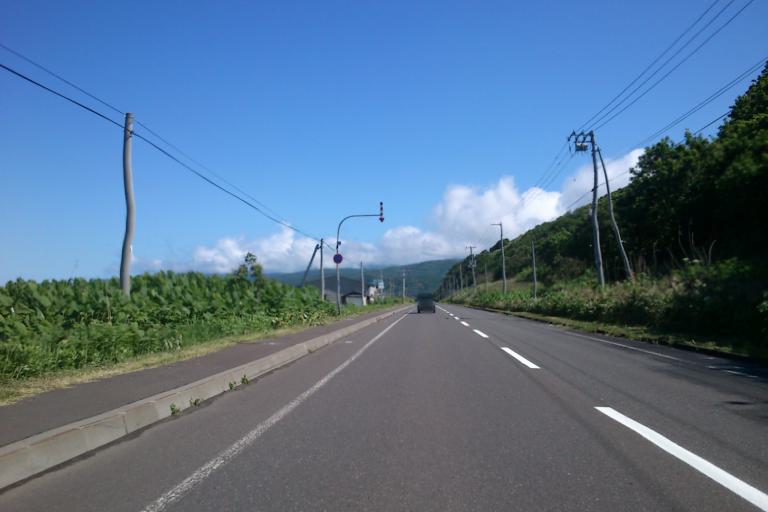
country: JP
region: Hokkaido
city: Ishikari
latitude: 43.5628
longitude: 141.3799
